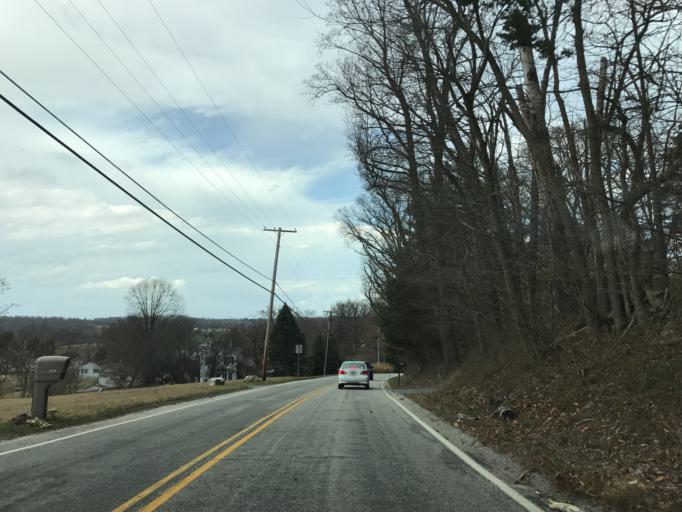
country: US
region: Maryland
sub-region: Harford County
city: South Bel Air
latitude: 39.5732
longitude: -76.2919
